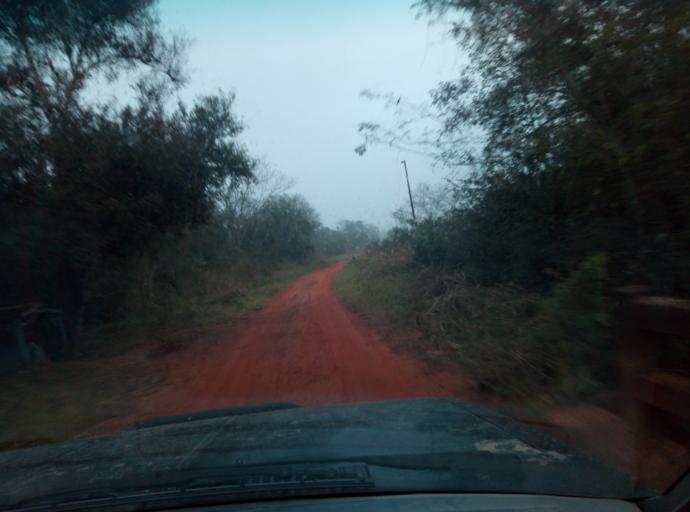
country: PY
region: Caaguazu
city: Doctor Cecilio Baez
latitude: -25.1589
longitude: -56.2567
